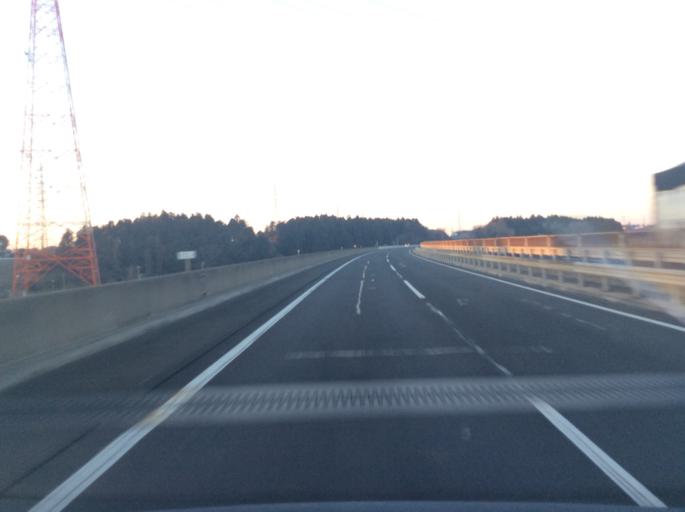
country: JP
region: Ibaraki
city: Funaishikawa
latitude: 36.4938
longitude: 140.5638
